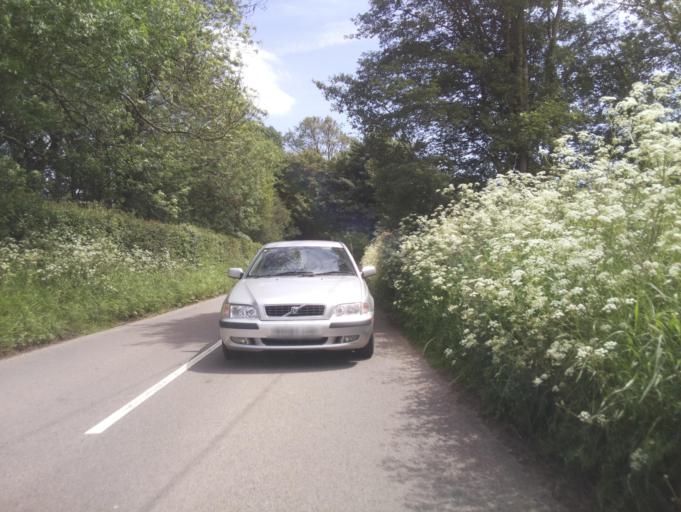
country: GB
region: England
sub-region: Herefordshire
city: Llanrothal
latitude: 51.8623
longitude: -2.8139
